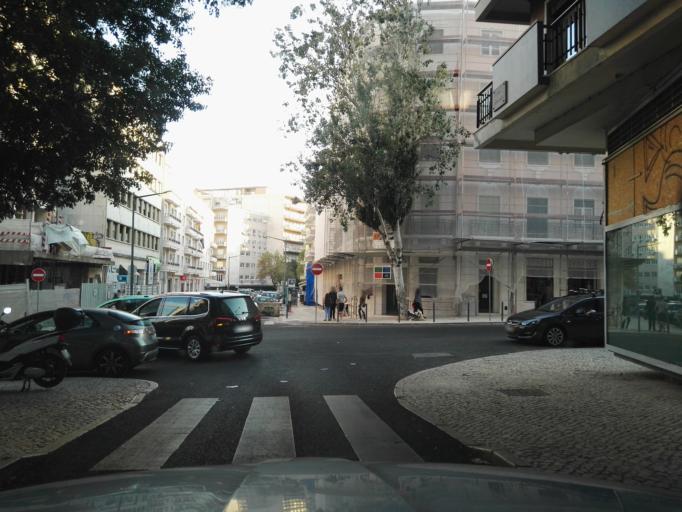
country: PT
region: Lisbon
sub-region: Lisbon
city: Lisbon
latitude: 38.7322
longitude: -9.1497
